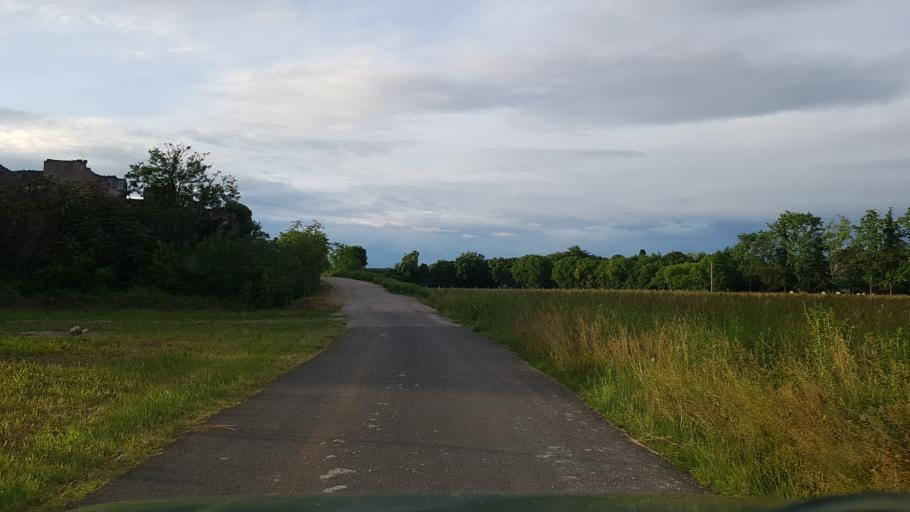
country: IT
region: Friuli Venezia Giulia
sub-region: Provincia di Gorizia
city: Sagrado
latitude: 45.8911
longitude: 13.4665
